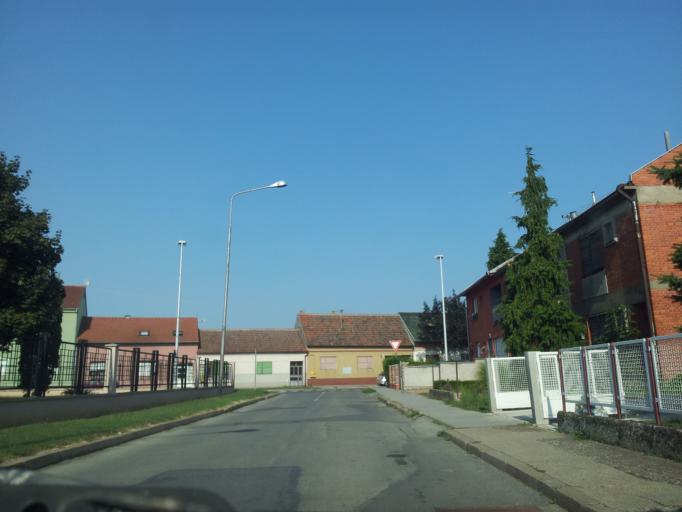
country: HR
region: Osjecko-Baranjska
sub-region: Grad Osijek
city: Osijek
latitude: 45.5470
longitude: 18.7145
